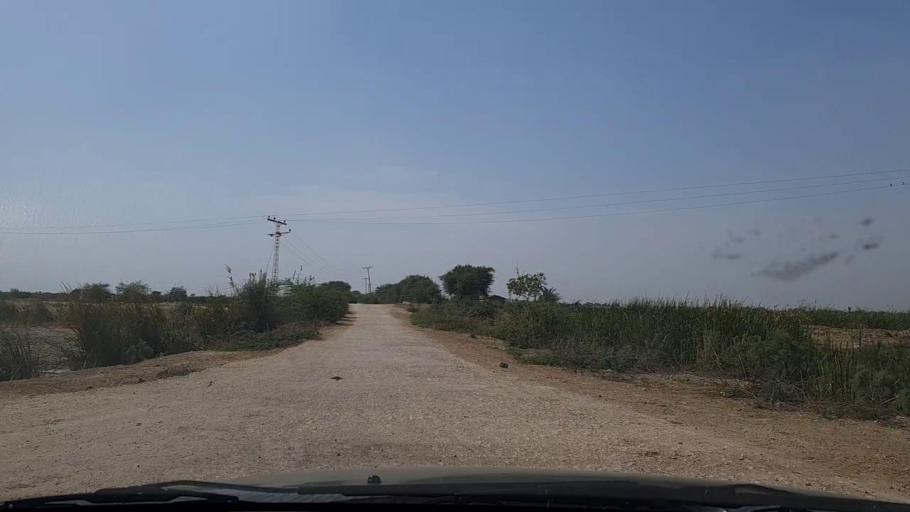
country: PK
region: Sindh
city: Mirpur Batoro
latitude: 24.6085
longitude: 68.2464
